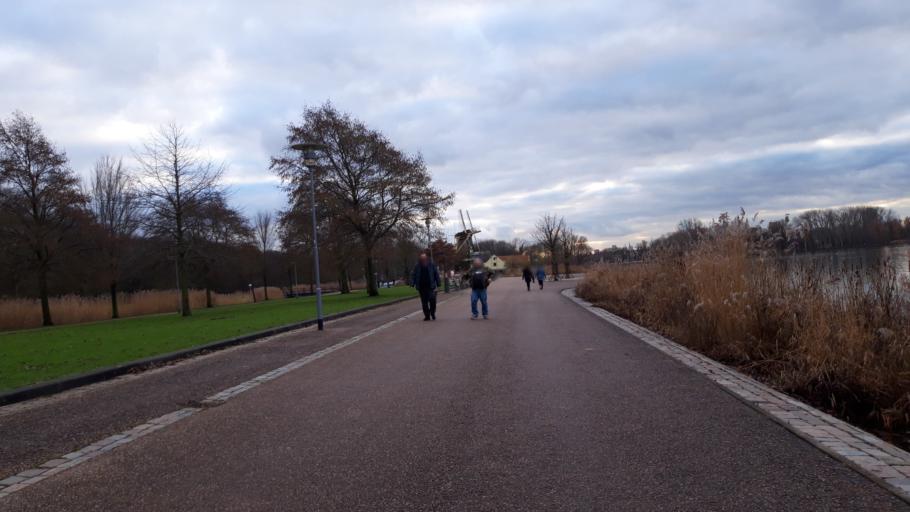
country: NL
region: South Holland
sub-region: Gemeente Rotterdam
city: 's-Gravenland
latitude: 51.9344
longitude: 4.5228
